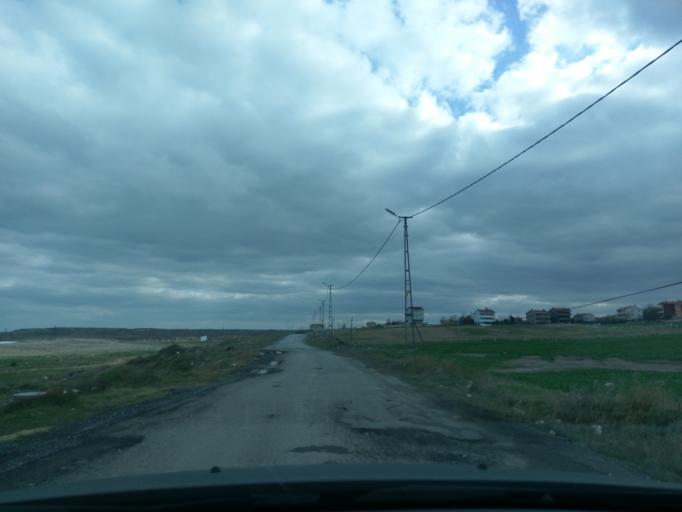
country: TR
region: Istanbul
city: Durusu
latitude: 41.3257
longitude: 28.7249
